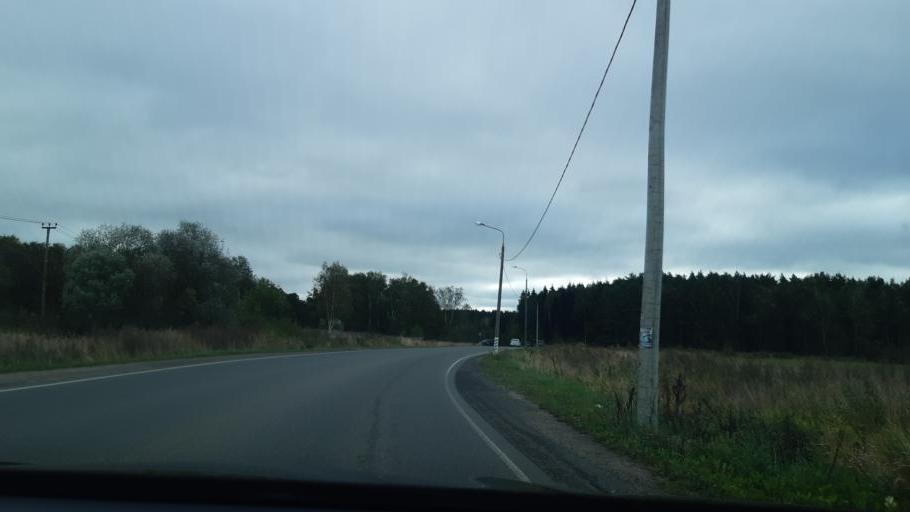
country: RU
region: Moskovskaya
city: Melikhovo
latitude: 55.1258
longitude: 37.6108
